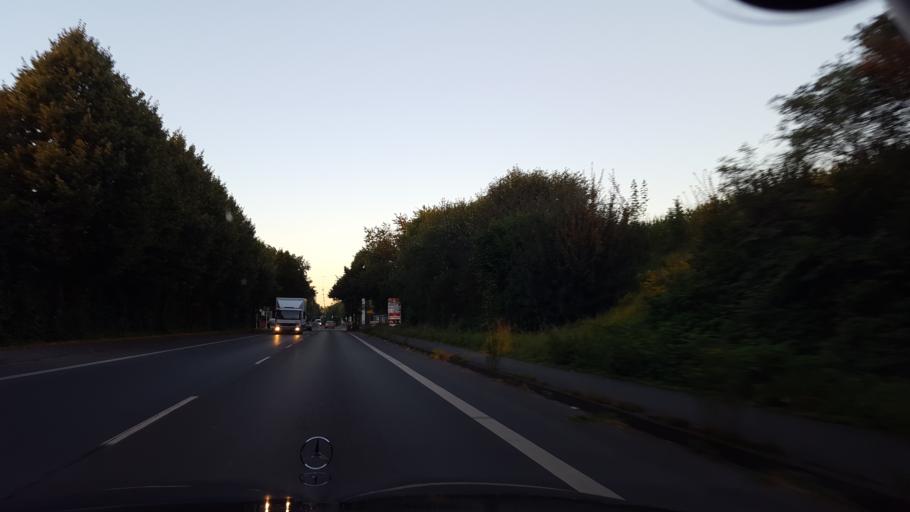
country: DE
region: North Rhine-Westphalia
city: Castrop-Rauxel
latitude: 51.6153
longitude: 7.3171
